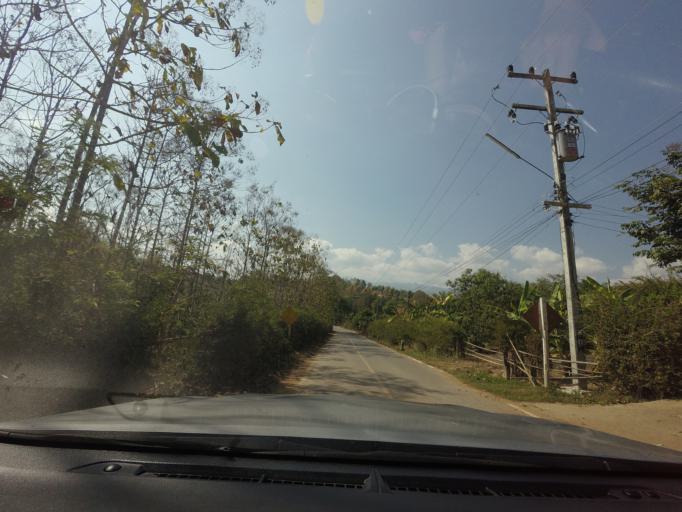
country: TH
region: Mae Hong Son
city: Wiang Nuea
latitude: 19.4017
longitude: 98.4435
